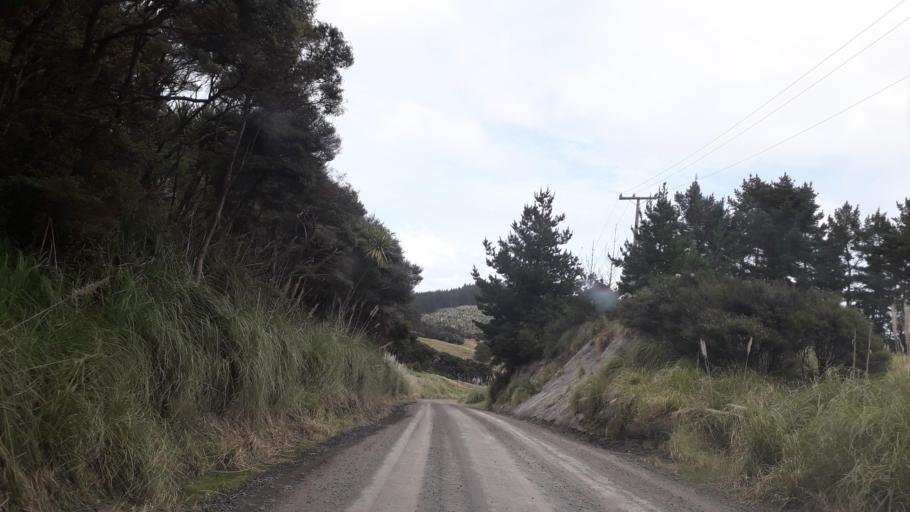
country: NZ
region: Northland
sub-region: Far North District
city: Ahipara
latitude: -35.4350
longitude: 173.3319
